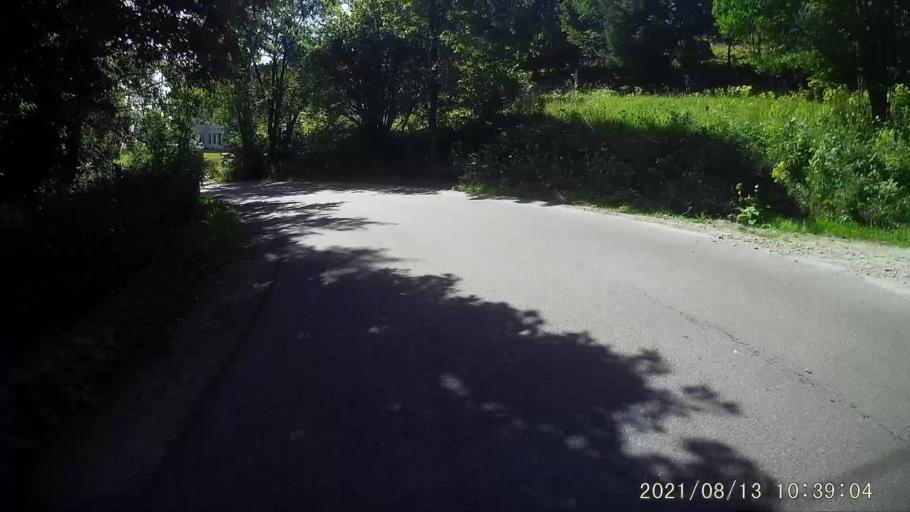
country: PL
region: Lower Silesian Voivodeship
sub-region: Powiat klodzki
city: Duszniki-Zdroj
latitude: 50.4432
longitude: 16.3433
